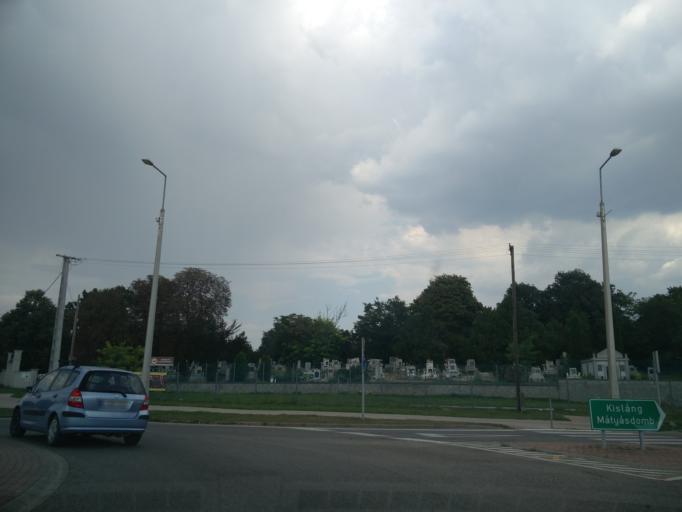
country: HU
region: Fejer
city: Polgardi
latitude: 47.0528
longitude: 18.3045
